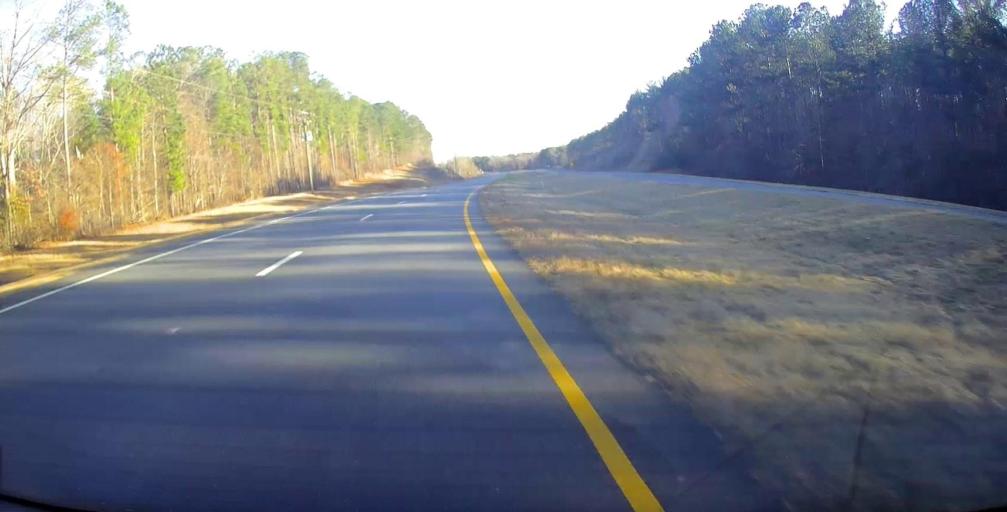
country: US
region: Georgia
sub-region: Upson County
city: Thomaston
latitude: 32.8242
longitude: -84.3002
